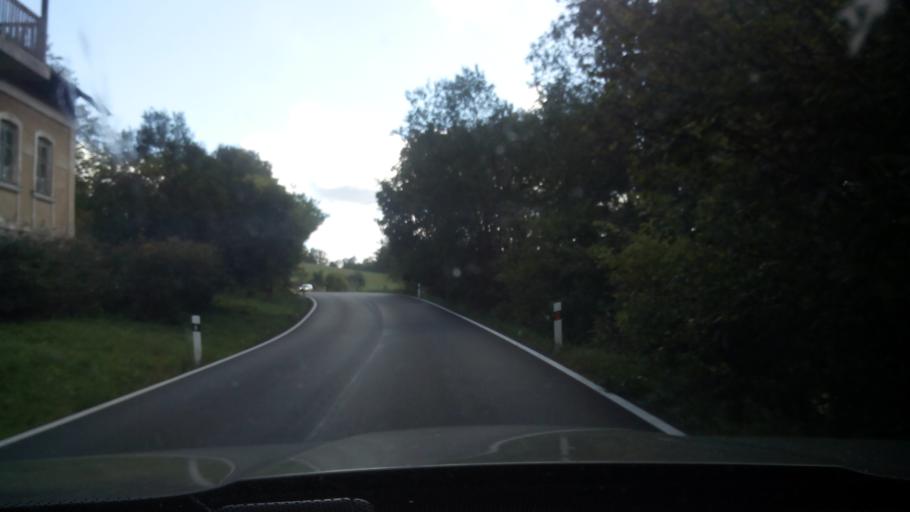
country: CZ
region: Plzensky
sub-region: Okres Klatovy
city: Kasperske Hory
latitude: 49.1303
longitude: 13.6127
